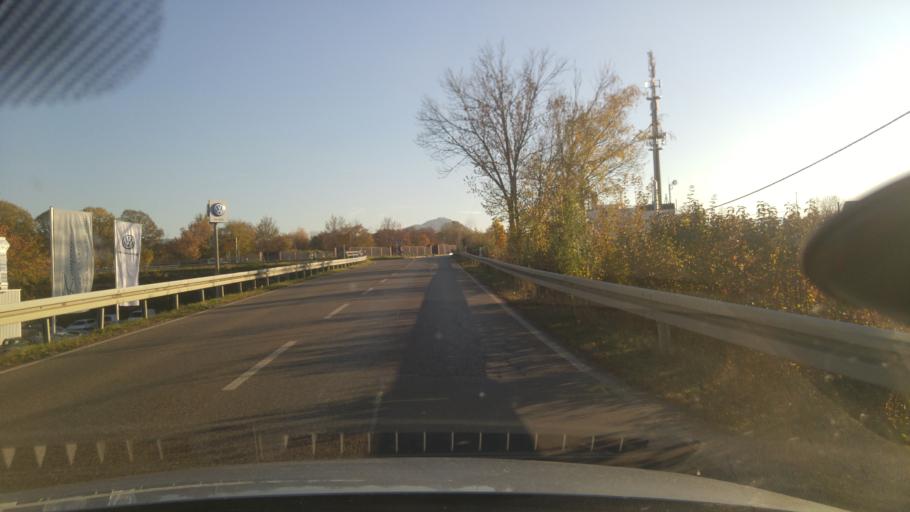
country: DE
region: Baden-Wuerttemberg
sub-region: Regierungsbezirk Stuttgart
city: Kirchheim unter Teck
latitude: 48.6368
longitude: 9.4555
